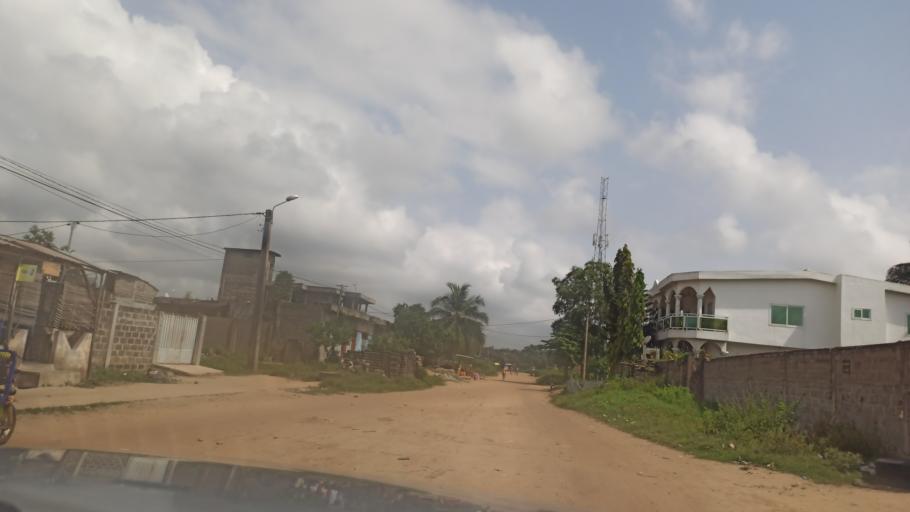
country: BJ
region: Queme
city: Porto-Novo
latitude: 6.4668
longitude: 2.6550
